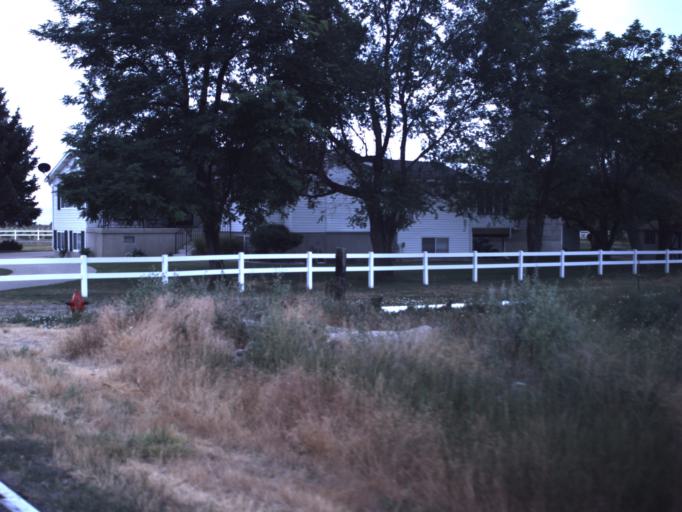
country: US
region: Utah
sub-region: Davis County
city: West Point
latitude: 41.0973
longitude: -112.1127
